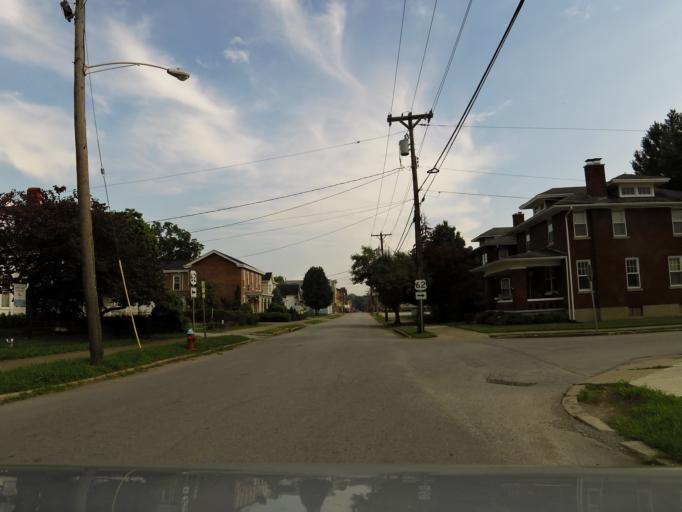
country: US
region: Kentucky
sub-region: Harrison County
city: Cynthiana
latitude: 38.3917
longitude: -84.2957
